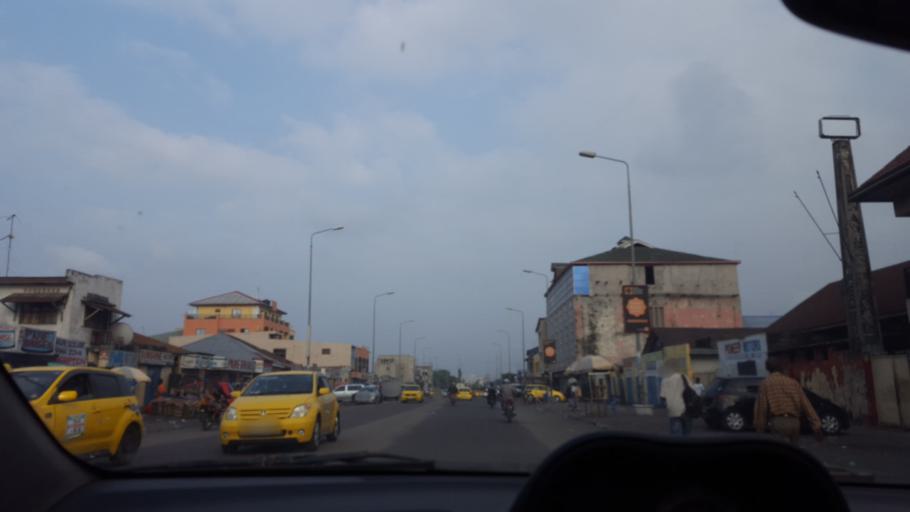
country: CD
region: Kinshasa
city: Kinshasa
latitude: -4.3387
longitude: 15.3072
